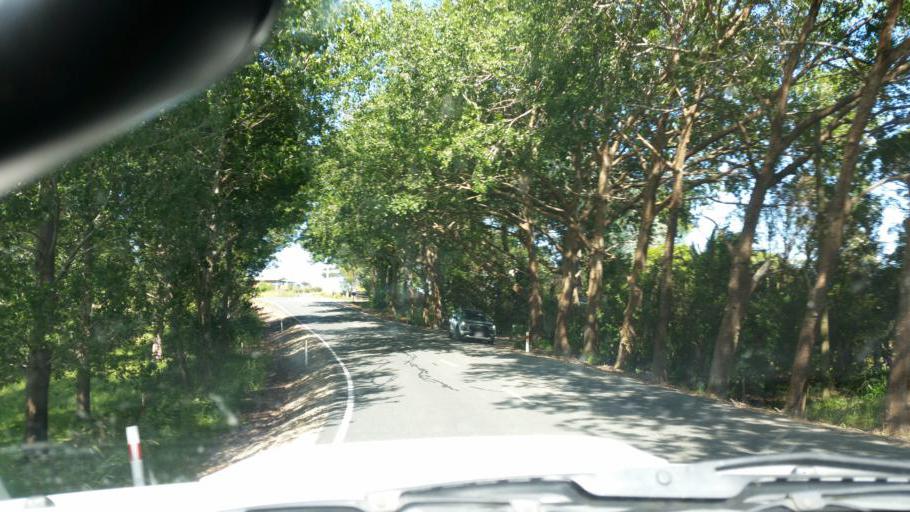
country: NZ
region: Auckland
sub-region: Auckland
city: Wellsford
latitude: -36.2186
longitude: 174.3837
